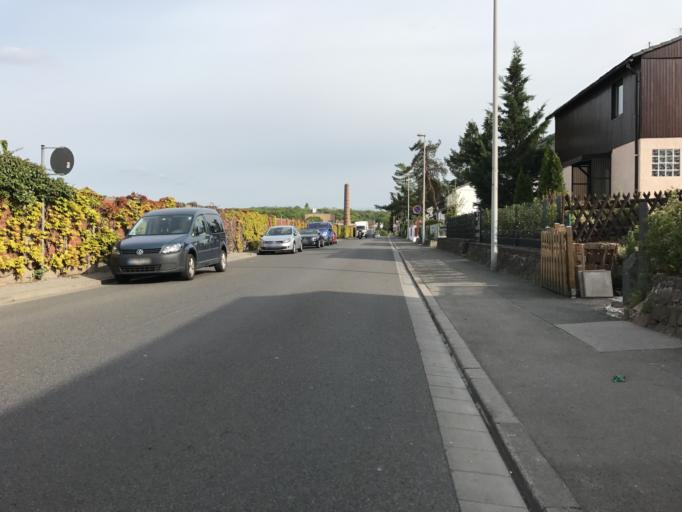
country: DE
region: Rheinland-Pfalz
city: Mainz
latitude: 50.0172
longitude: 8.2301
